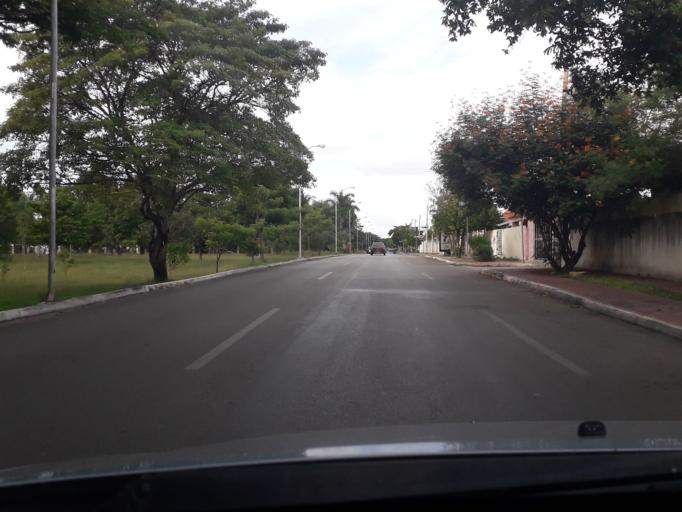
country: MX
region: Yucatan
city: Merida
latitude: 20.9758
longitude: -89.6631
